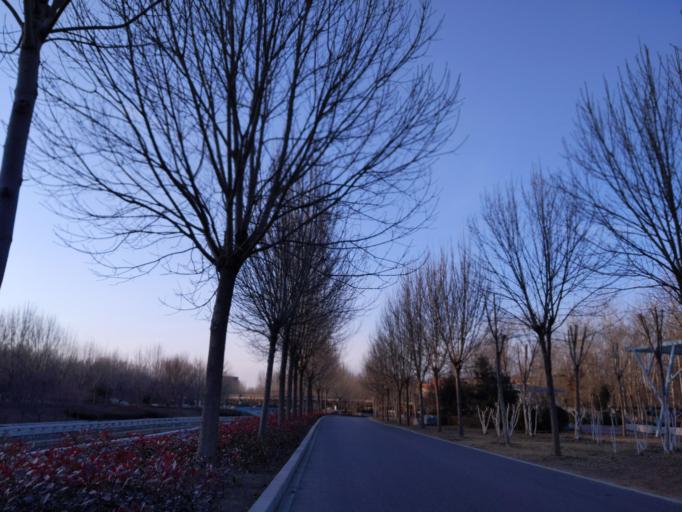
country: CN
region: Henan Sheng
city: Puyang
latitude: 35.7686
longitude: 114.9990
